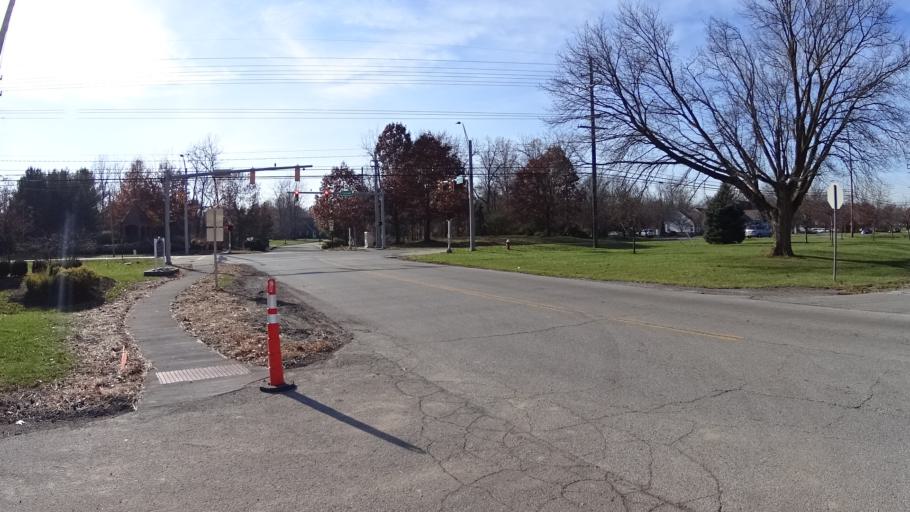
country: US
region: Ohio
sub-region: Lorain County
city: Avon
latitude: 41.4576
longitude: -82.0400
